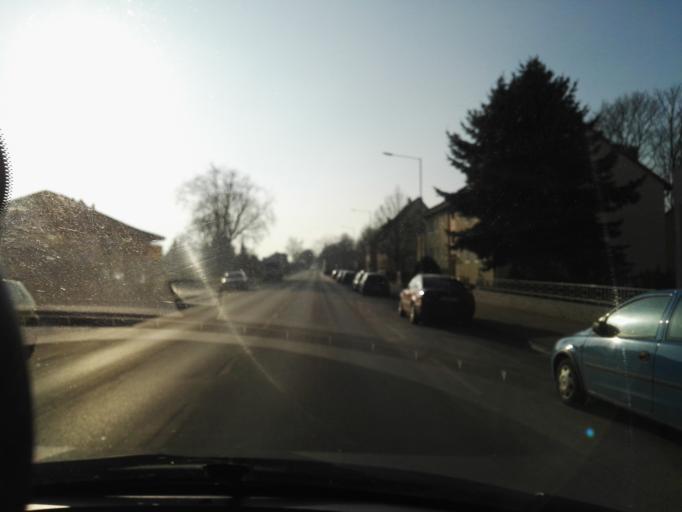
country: DE
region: Lower Saxony
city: Sarstedt
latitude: 52.2236
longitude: 9.8404
